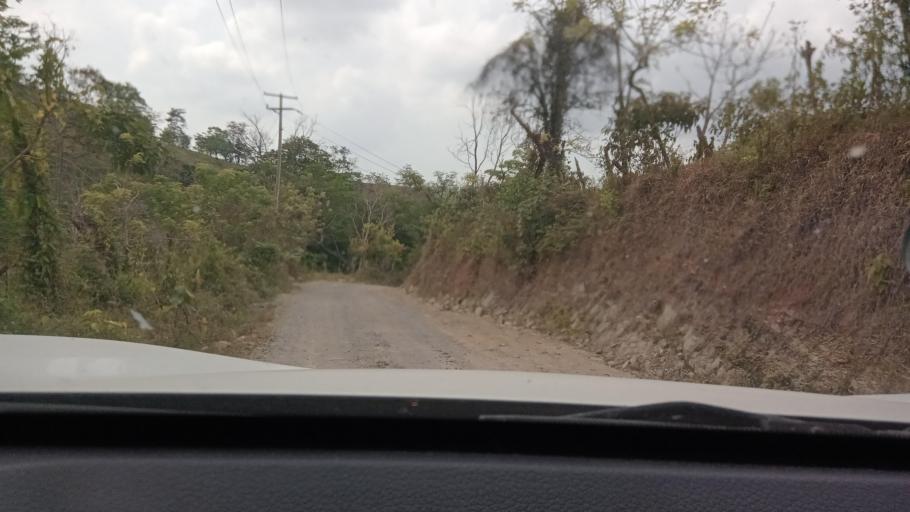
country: MX
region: Tabasco
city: Chontalpa
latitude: 17.5034
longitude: -93.6441
